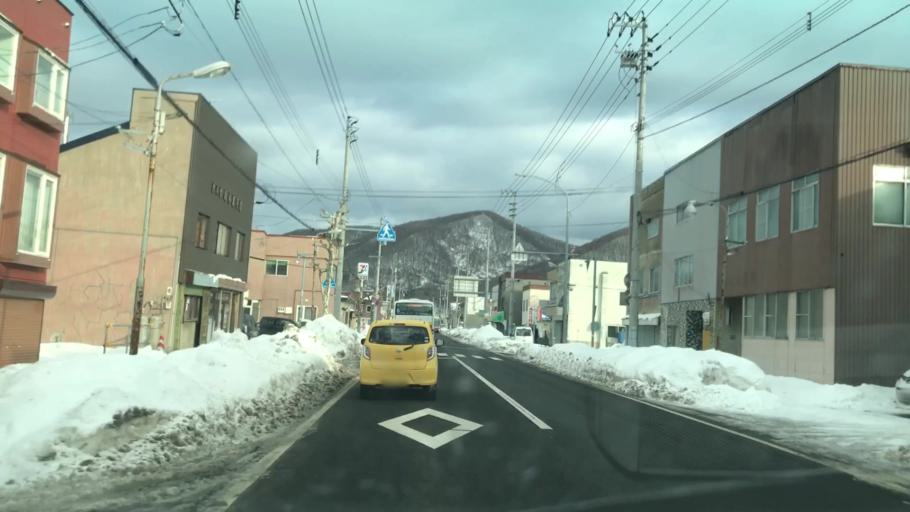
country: JP
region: Hokkaido
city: Yoichi
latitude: 43.2053
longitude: 140.7714
